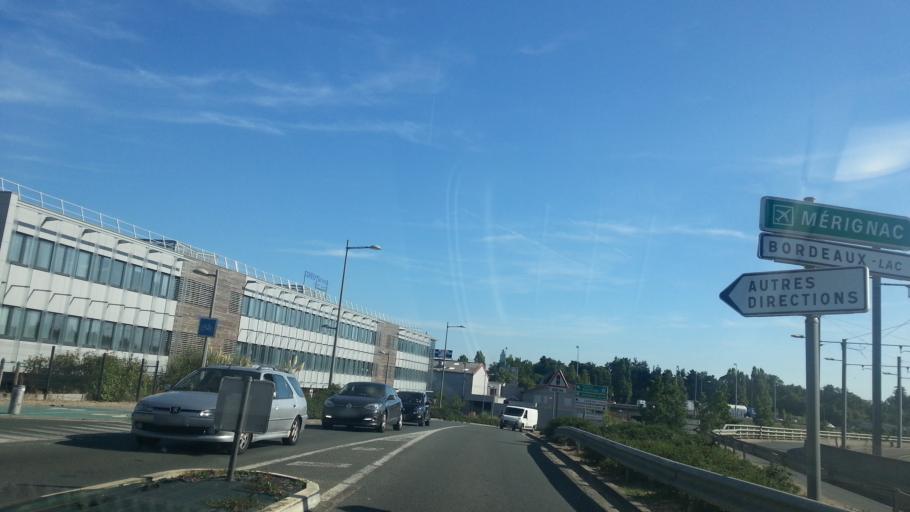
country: FR
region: Aquitaine
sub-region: Departement de la Gironde
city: Lormont
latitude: 44.8865
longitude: -0.5174
